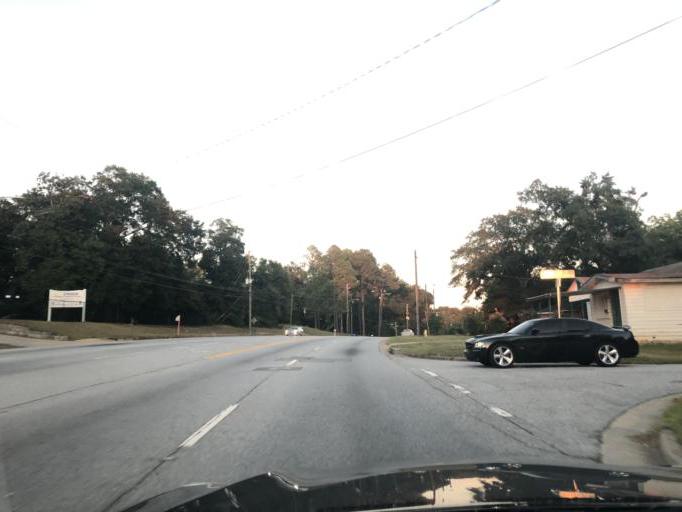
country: US
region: Georgia
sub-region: Muscogee County
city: Columbus
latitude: 32.4677
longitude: -84.9063
